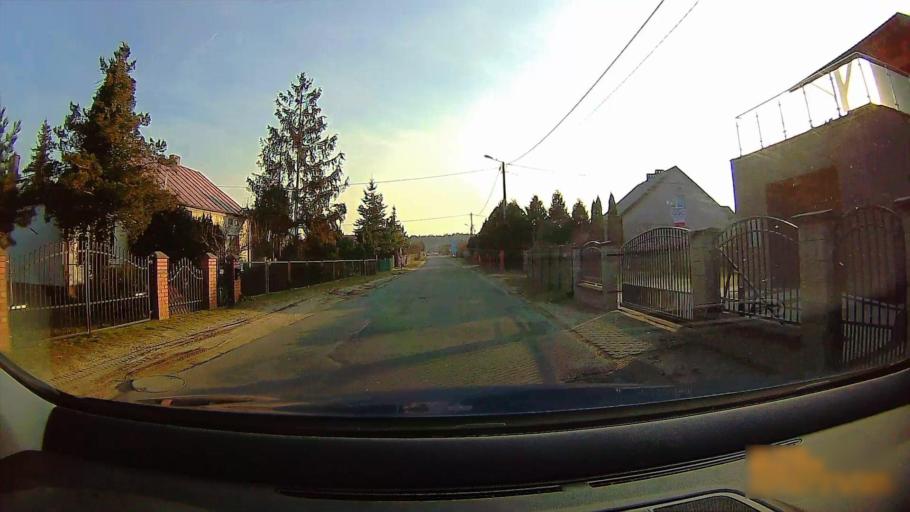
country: PL
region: Greater Poland Voivodeship
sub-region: Konin
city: Konin
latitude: 52.1898
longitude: 18.3327
